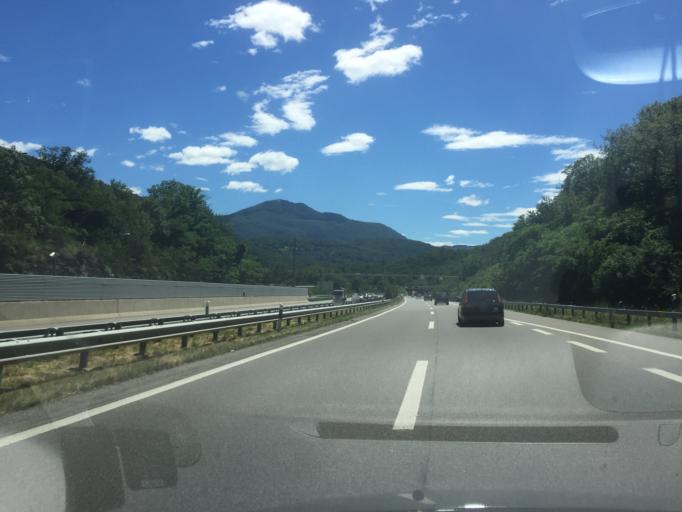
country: CH
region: Ticino
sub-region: Lugano District
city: Gravesano
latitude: 46.0777
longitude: 8.9229
